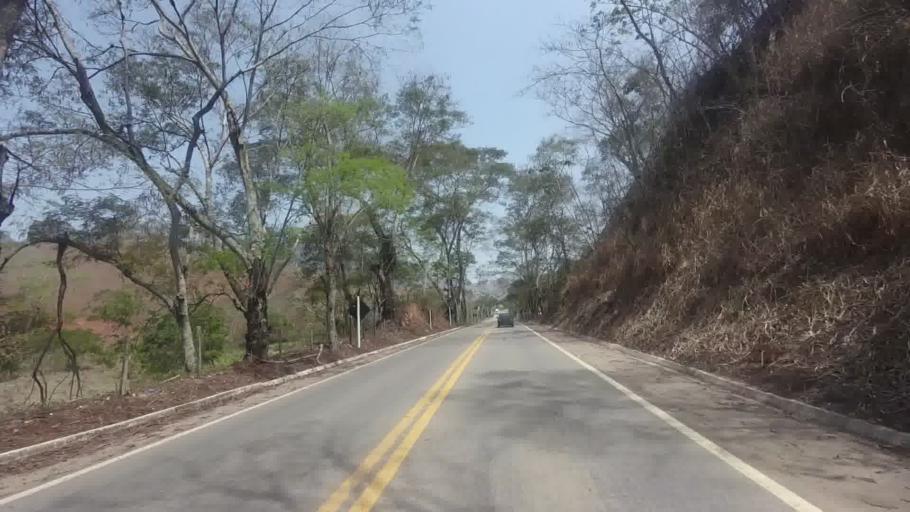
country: BR
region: Espirito Santo
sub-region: Mimoso Do Sul
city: Mimoso do Sul
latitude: -20.9369
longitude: -41.3265
